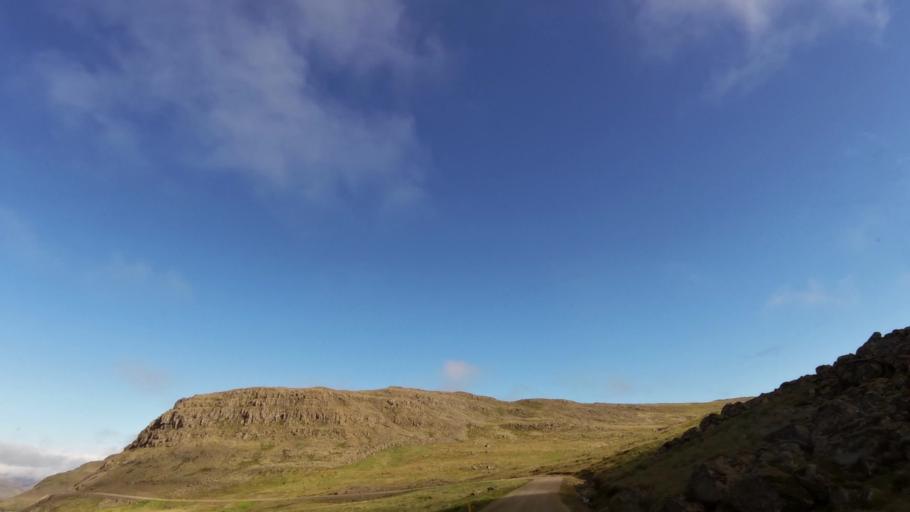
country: IS
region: West
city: Olafsvik
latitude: 65.5629
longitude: -24.0360
